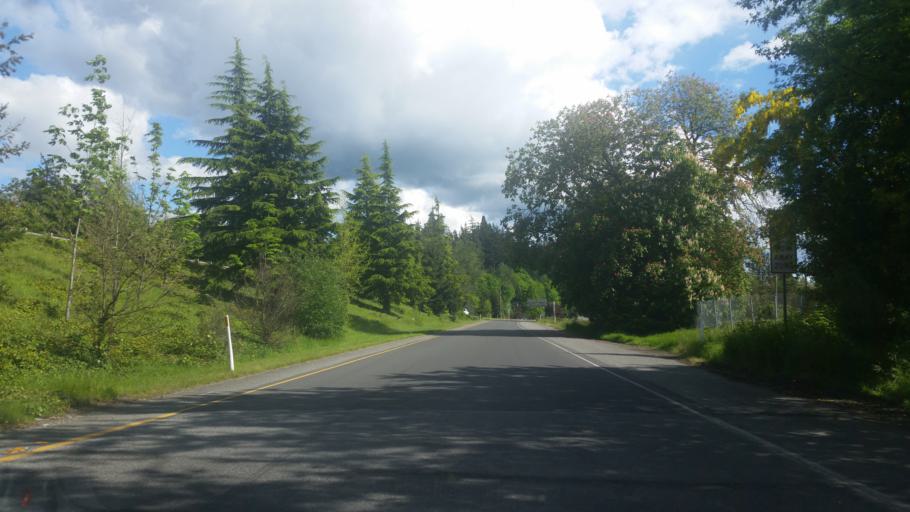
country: US
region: Washington
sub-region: Skagit County
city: Mount Vernon
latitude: 48.4172
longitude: -122.3334
